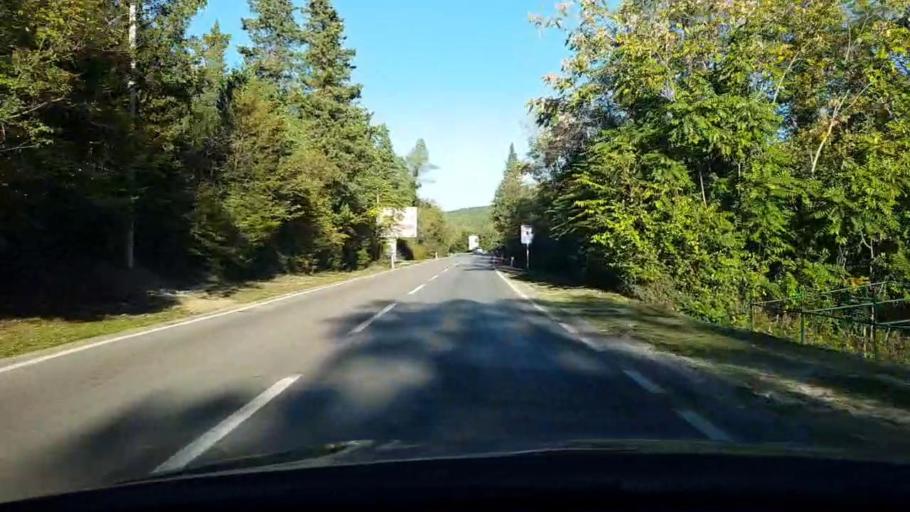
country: ME
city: Igalo
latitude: 42.4776
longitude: 18.4625
